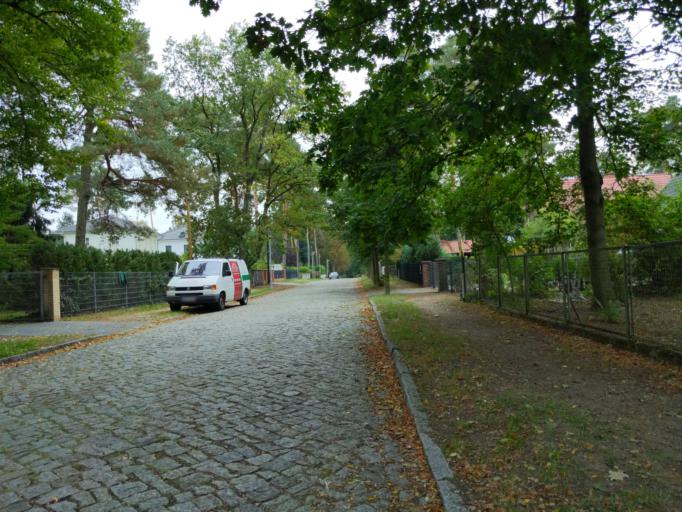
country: DE
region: Brandenburg
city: Michendorf
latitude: 52.3334
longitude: 13.0488
